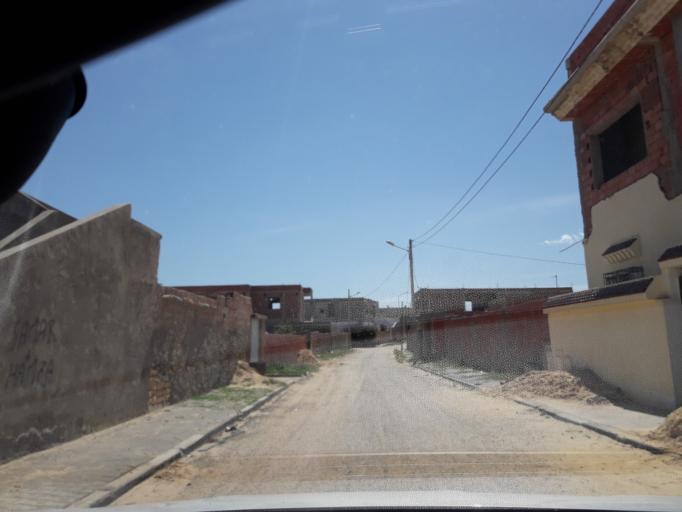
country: TN
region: Safaqis
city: Sfax
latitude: 34.7422
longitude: 10.5197
